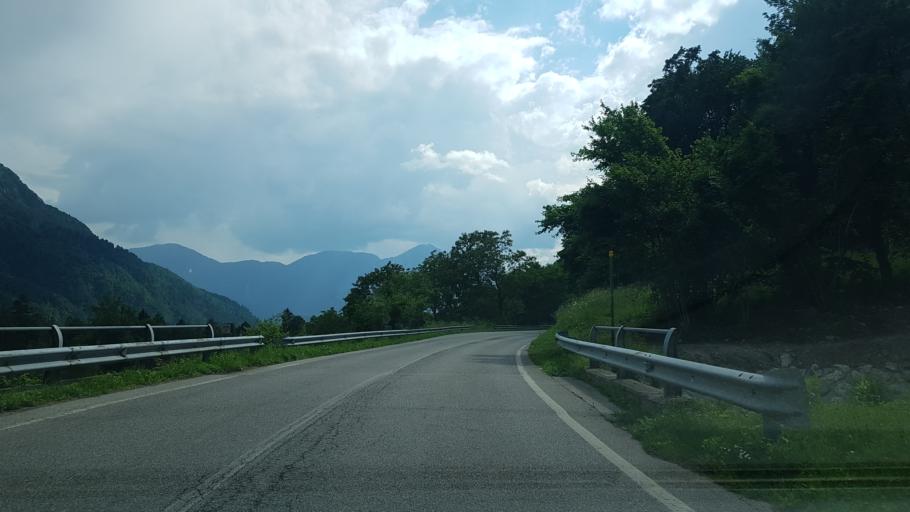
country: IT
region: Friuli Venezia Giulia
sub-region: Provincia di Udine
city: Zuglio
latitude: 46.4389
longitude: 13.0278
